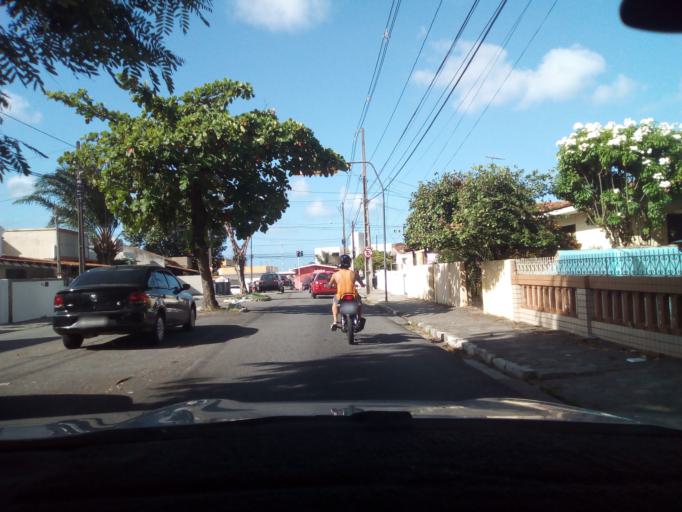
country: BR
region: Paraiba
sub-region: Joao Pessoa
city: Joao Pessoa
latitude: -7.1162
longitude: -34.8742
